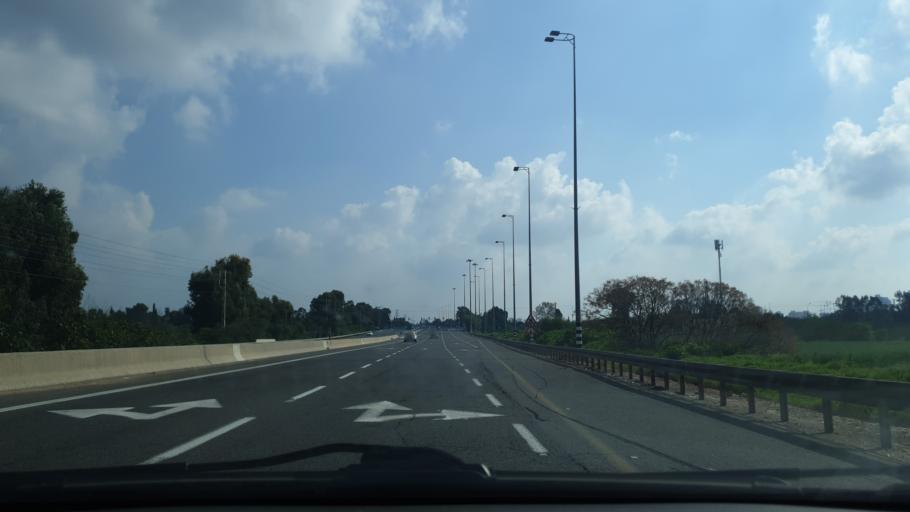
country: IL
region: Central District
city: Ramla
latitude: 31.9551
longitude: 34.8547
